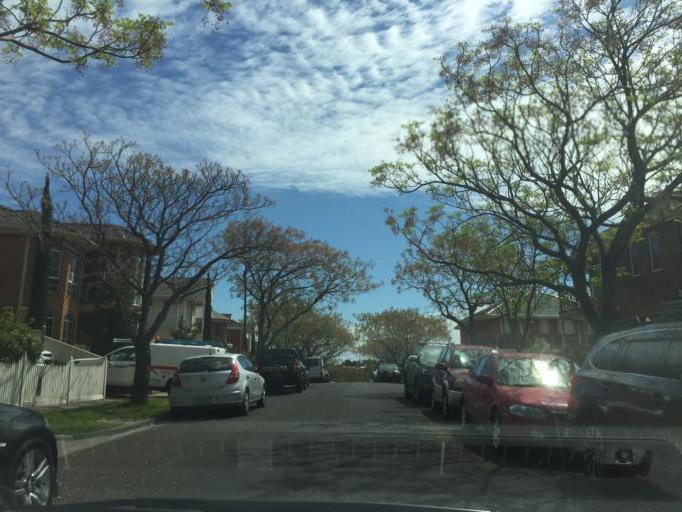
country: AU
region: Victoria
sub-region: Maribyrnong
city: Maidstone
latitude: -37.7739
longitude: 144.8744
